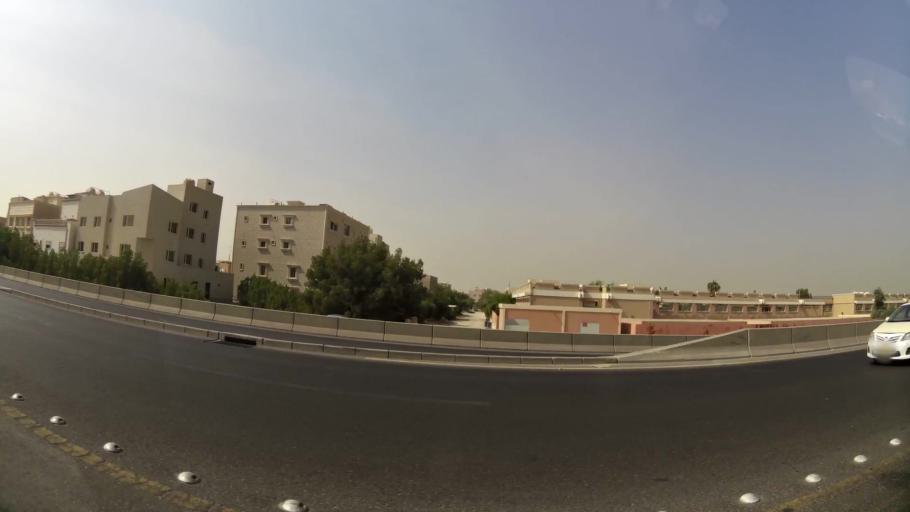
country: KW
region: Al Farwaniyah
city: Al Farwaniyah
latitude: 29.2869
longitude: 47.9482
